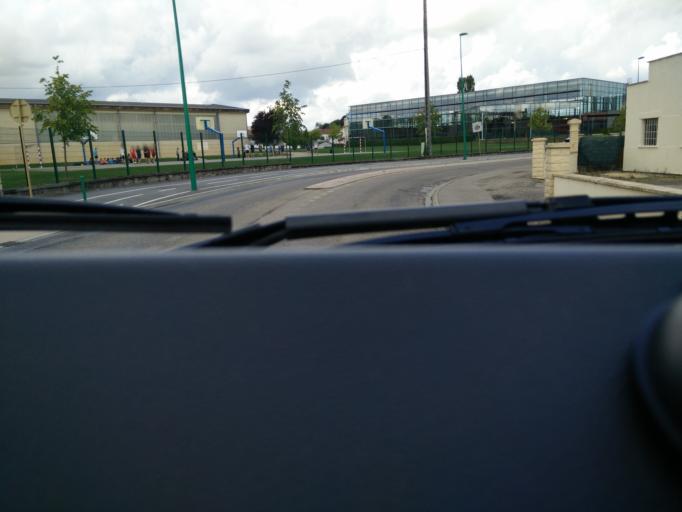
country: FR
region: Lorraine
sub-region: Departement de la Meuse
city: Verdun
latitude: 49.1595
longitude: 5.3933
